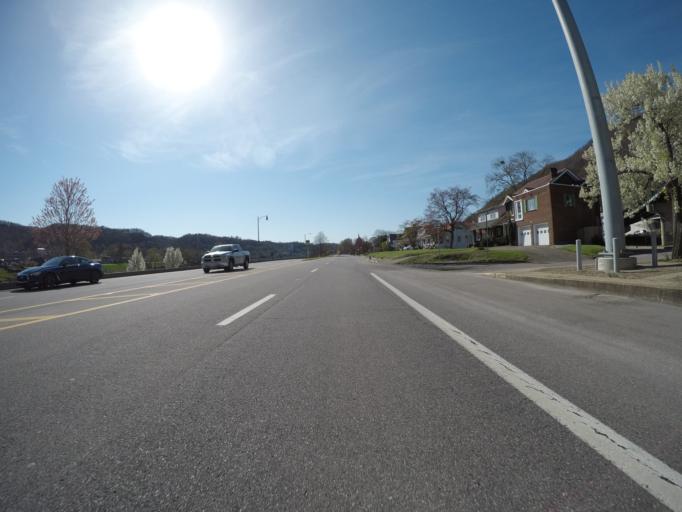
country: US
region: West Virginia
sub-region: Kanawha County
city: Charleston
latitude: 38.3342
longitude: -81.5981
